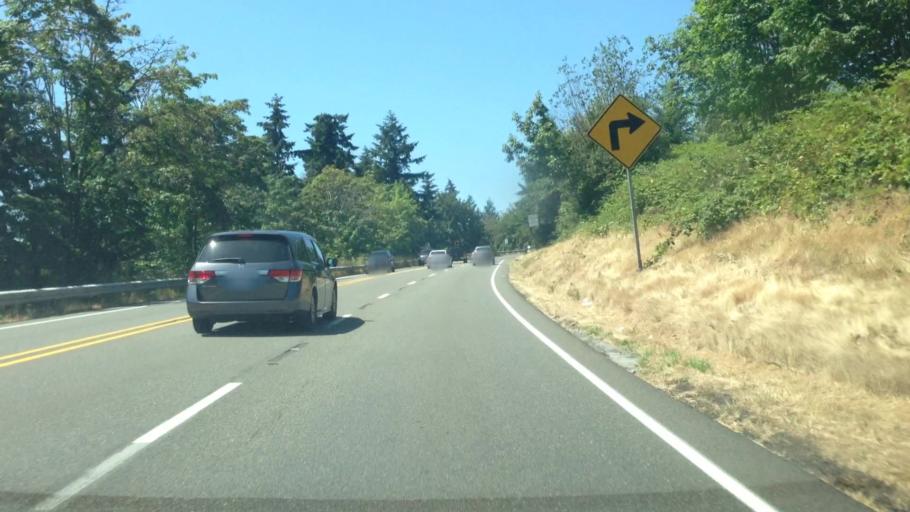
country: US
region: Washington
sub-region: Pierce County
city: North Puyallup
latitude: 47.2162
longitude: -122.2962
